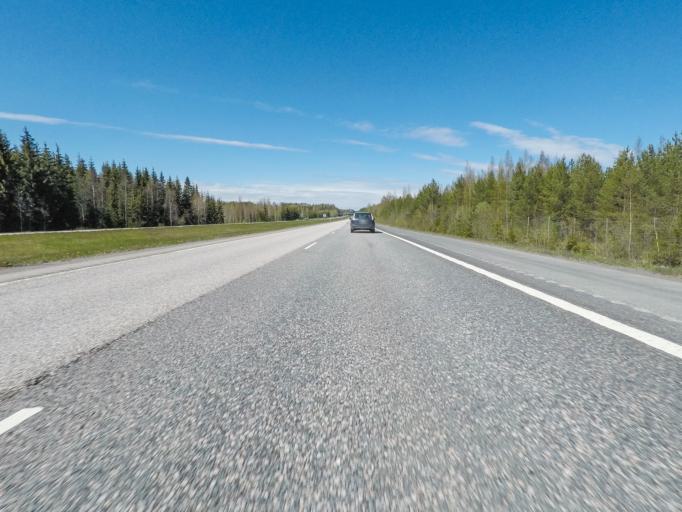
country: FI
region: Haeme
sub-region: Riihimaeki
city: Riihimaeki
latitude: 60.6699
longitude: 24.7801
